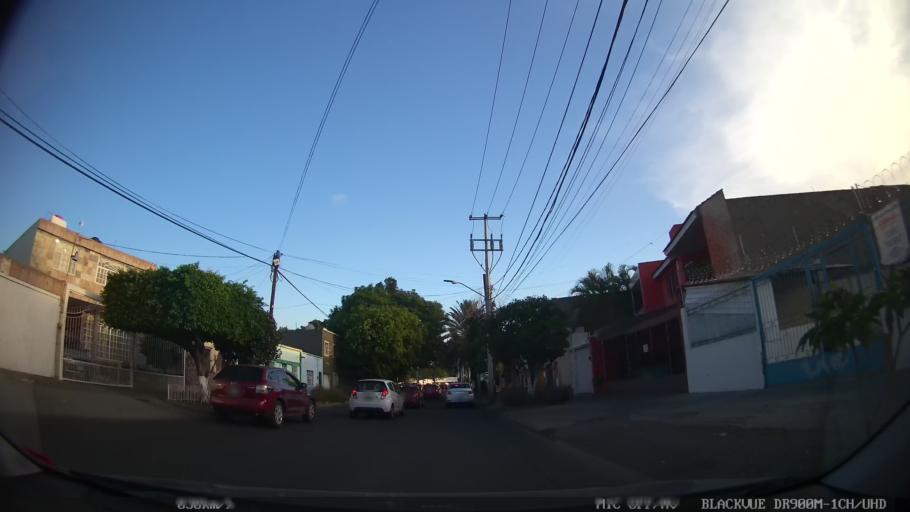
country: MX
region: Jalisco
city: Tlaquepaque
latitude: 20.6582
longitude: -103.3187
